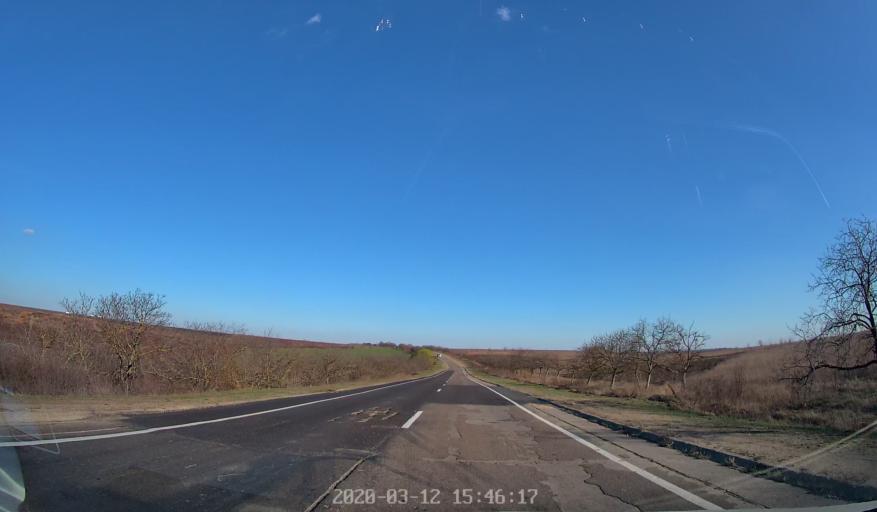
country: MD
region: Chisinau
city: Stauceni
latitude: 47.1005
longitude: 28.8900
